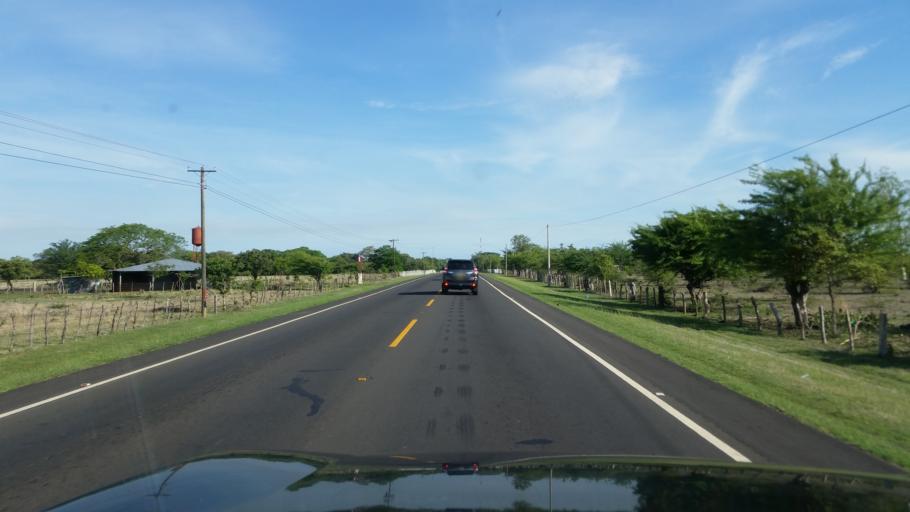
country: NI
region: Leon
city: La Paz Centro
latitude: 12.2869
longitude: -86.7574
